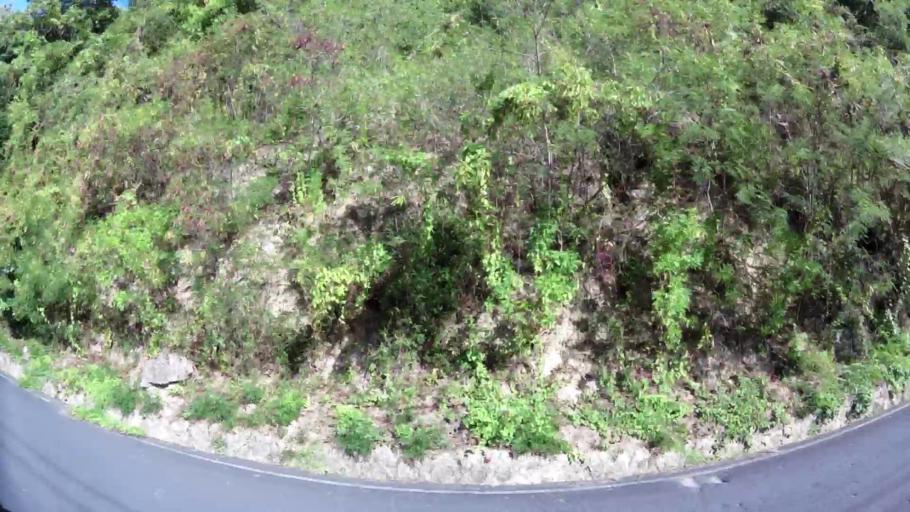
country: LC
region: Soufriere
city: Soufriere
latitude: 13.8591
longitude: -61.0609
